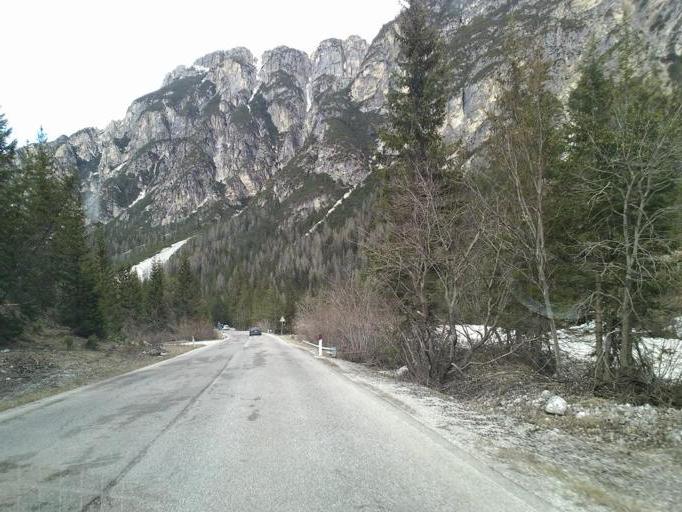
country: IT
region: Veneto
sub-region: Provincia di Belluno
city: Cortina d'Ampezzo
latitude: 46.5992
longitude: 12.2423
